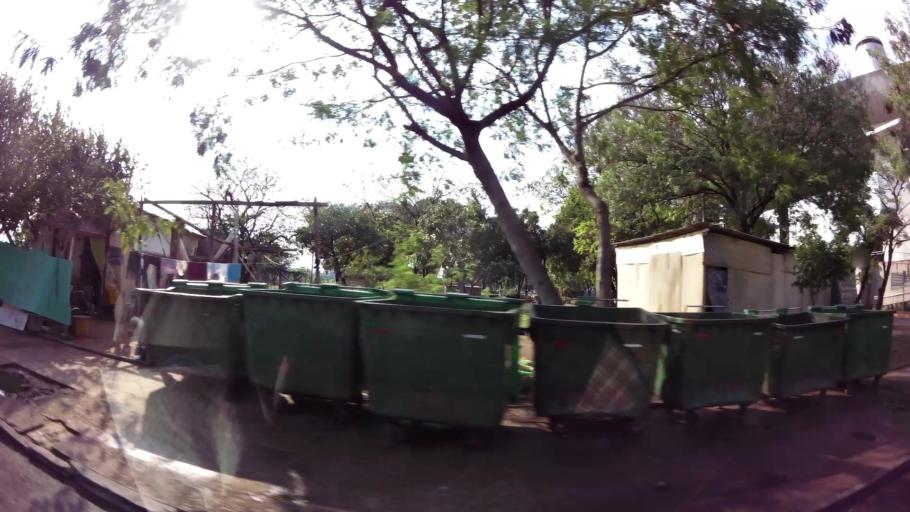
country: PY
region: Asuncion
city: Asuncion
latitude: -25.2782
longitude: -57.6359
